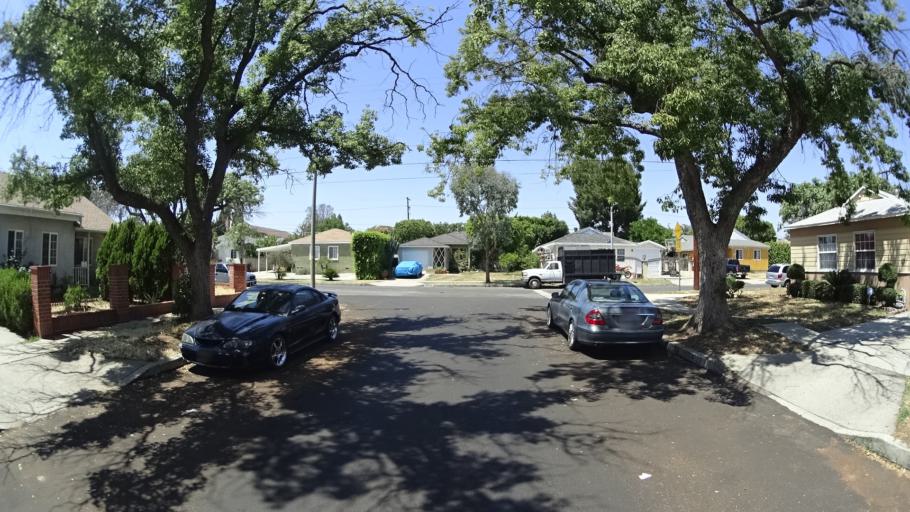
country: US
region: California
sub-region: Los Angeles County
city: Van Nuys
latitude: 34.2205
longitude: -118.4390
